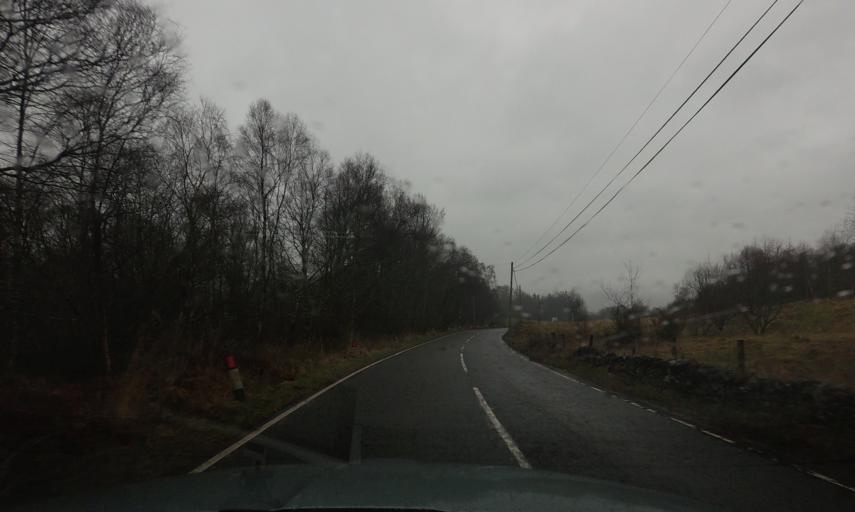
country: GB
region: Scotland
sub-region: Stirling
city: Balfron
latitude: 56.1401
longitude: -4.3618
